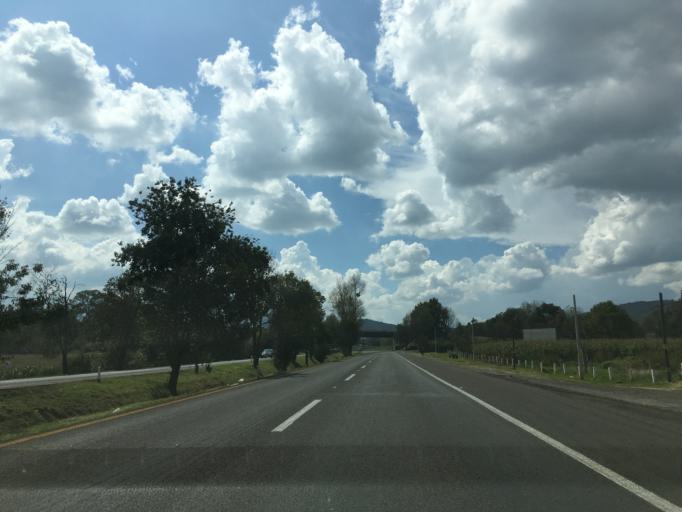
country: MX
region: Michoacan
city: Huiramba
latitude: 19.5456
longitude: -101.4476
